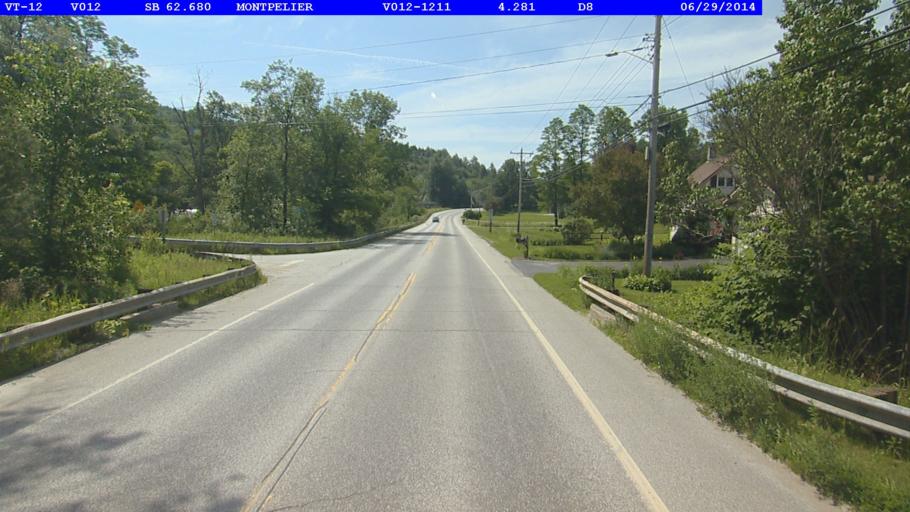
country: US
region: Vermont
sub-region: Washington County
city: Montpelier
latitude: 44.3032
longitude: -72.5793
